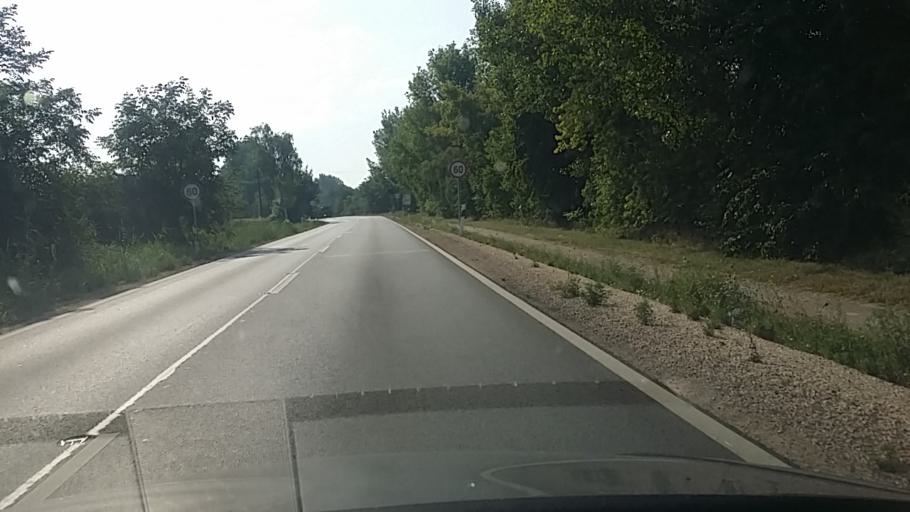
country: HU
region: Bekes
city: Szarvas
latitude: 46.8248
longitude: 20.6597
